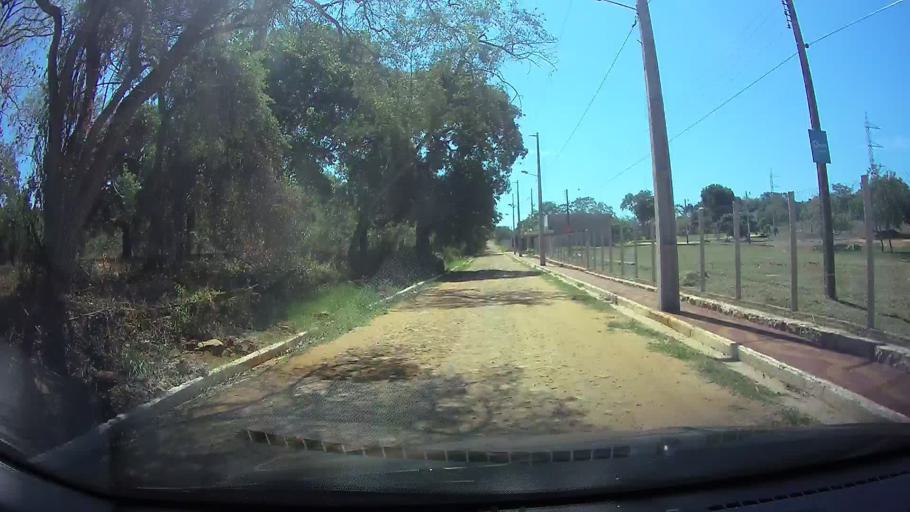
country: PY
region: Central
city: Limpio
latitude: -25.2341
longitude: -57.4381
